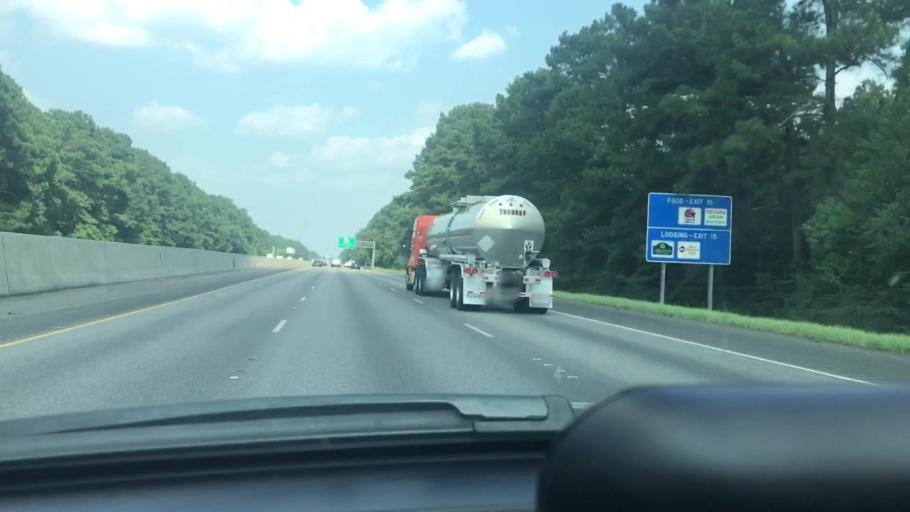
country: US
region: Louisiana
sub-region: Livingston Parish
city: Walker
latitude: 30.4669
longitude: -90.8863
